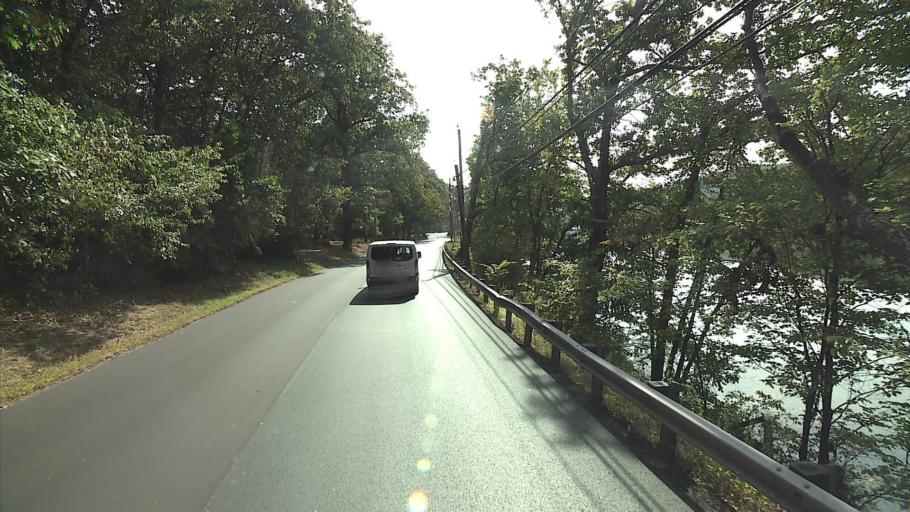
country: US
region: Connecticut
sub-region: Fairfield County
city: Shelton
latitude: 41.3475
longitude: -73.1252
